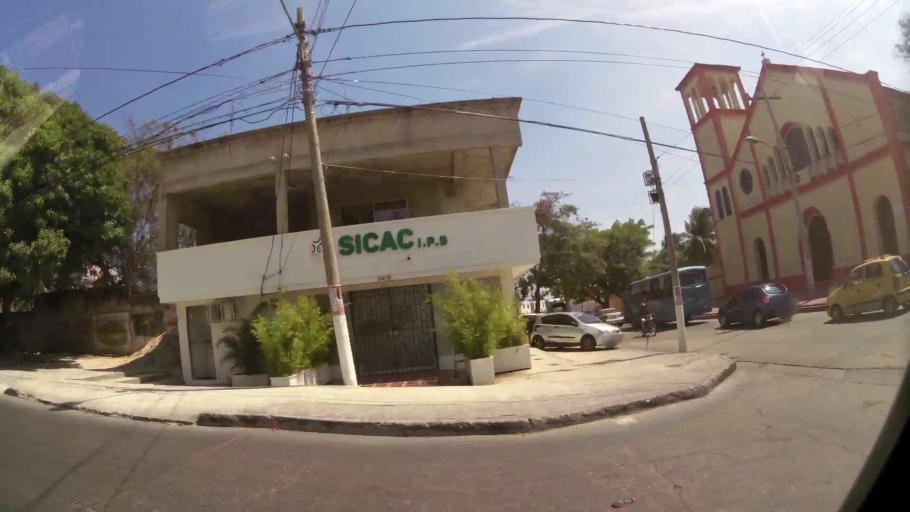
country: CO
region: Atlantico
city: Barranquilla
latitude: 10.9685
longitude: -74.8014
